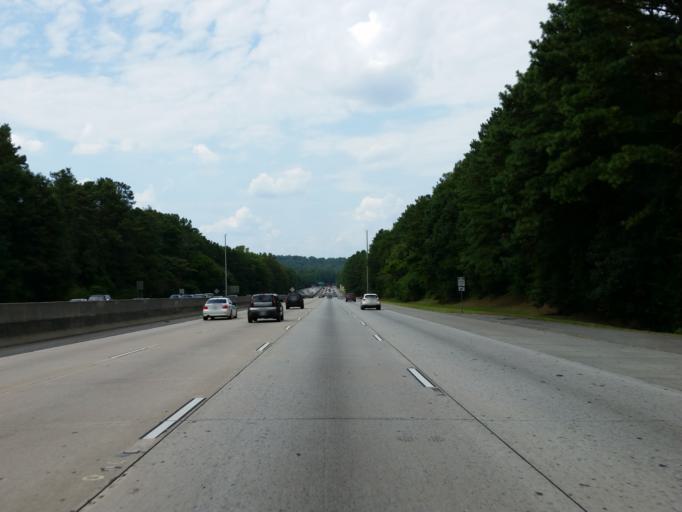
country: US
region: Georgia
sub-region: Fulton County
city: Roswell
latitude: 33.9936
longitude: -84.3377
